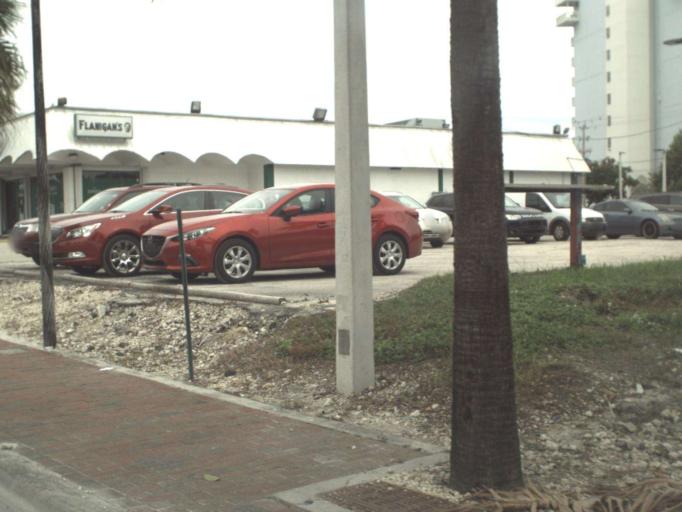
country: US
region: Florida
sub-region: Miami-Dade County
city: Biscayne Park
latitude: 25.8973
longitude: -80.1613
